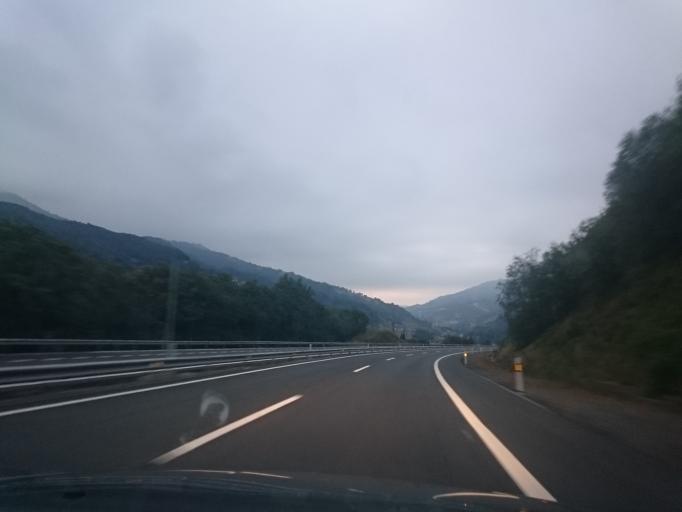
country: ES
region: Asturias
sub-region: Province of Asturias
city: Pola de Lena
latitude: 43.0944
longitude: -5.8227
